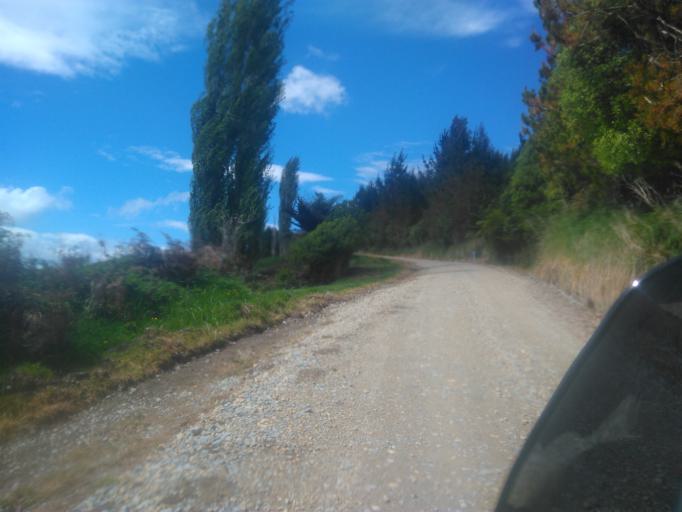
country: NZ
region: Hawke's Bay
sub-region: Wairoa District
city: Wairoa
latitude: -38.7702
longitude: 177.6015
